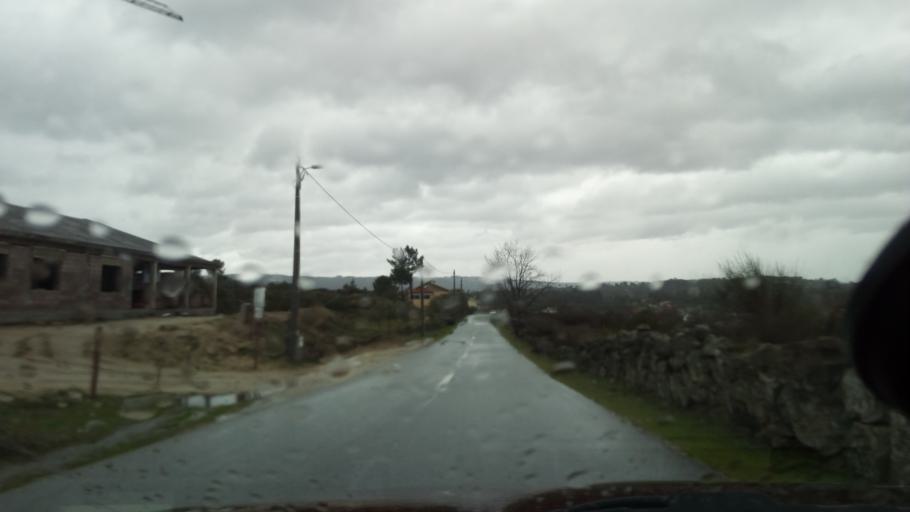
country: PT
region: Guarda
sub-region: Fornos de Algodres
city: Fornos de Algodres
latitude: 40.5811
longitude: -7.5115
